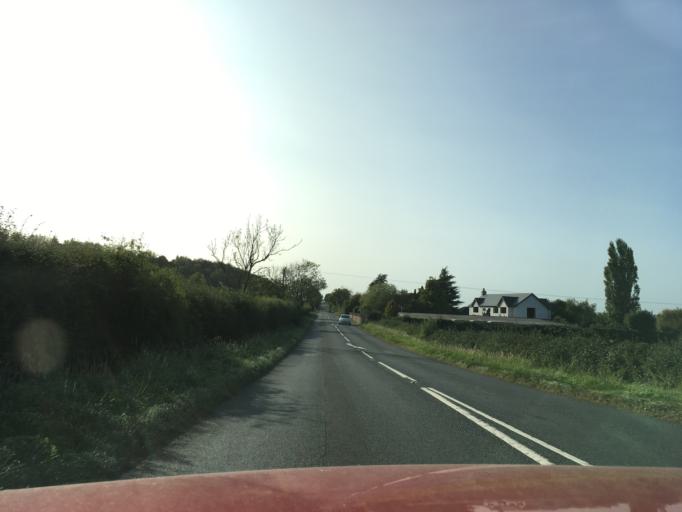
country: GB
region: England
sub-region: Gloucestershire
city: Gloucester
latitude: 51.9609
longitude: -2.2567
